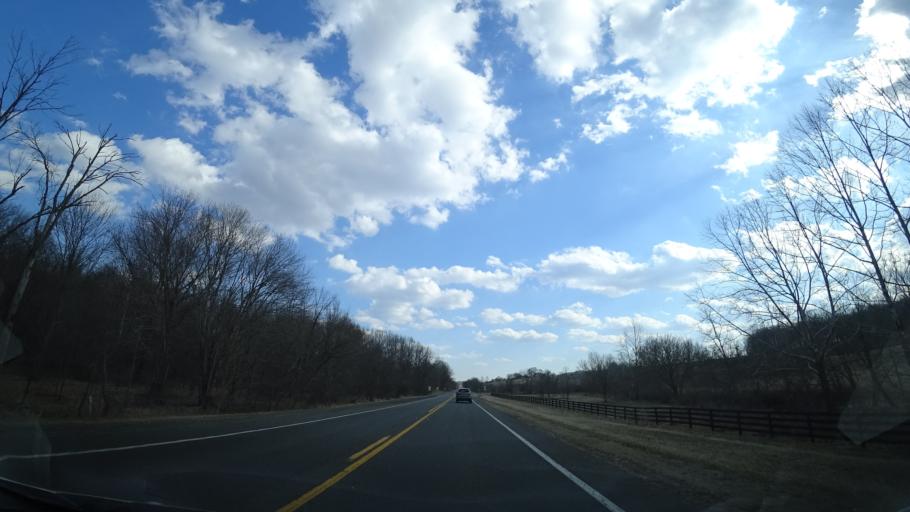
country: US
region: Virginia
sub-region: Fauquier County
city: Marshall
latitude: 38.9387
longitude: -77.9348
